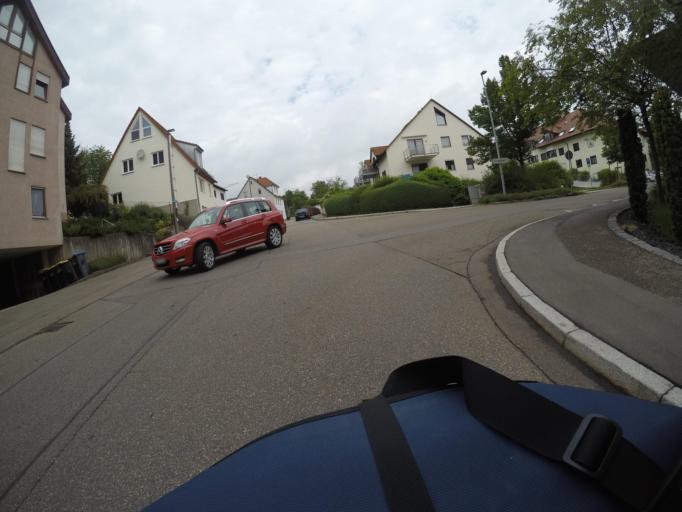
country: DE
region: Baden-Wuerttemberg
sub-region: Regierungsbezirk Stuttgart
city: Ditzingen
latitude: 48.8287
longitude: 9.0620
